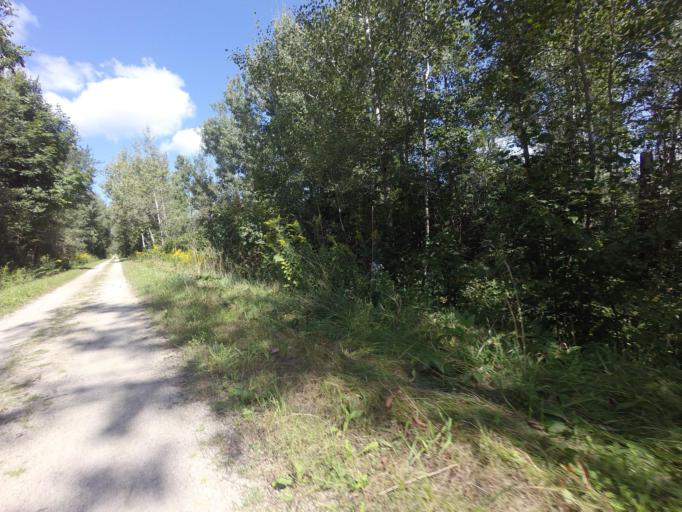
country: CA
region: Ontario
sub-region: Wellington County
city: Guelph
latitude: 43.7482
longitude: -80.3180
